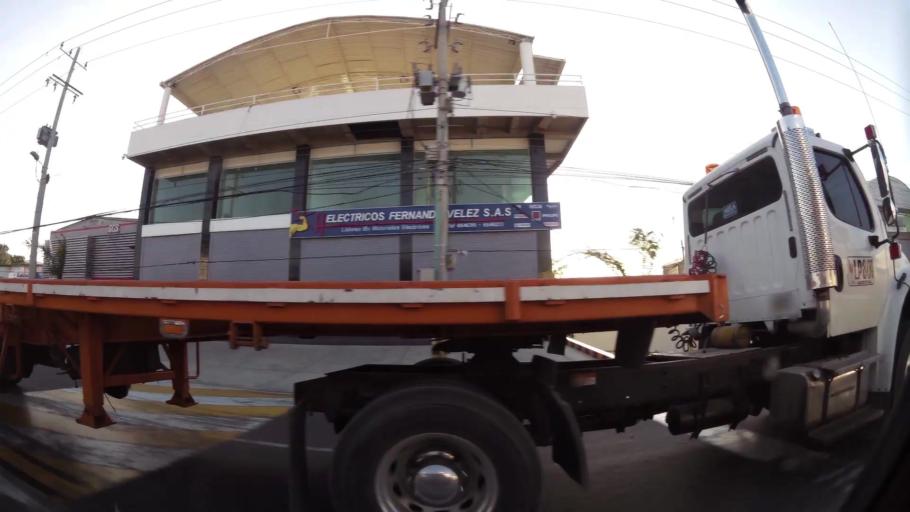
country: CO
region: Bolivar
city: Cartagena
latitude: 10.4014
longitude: -75.5193
